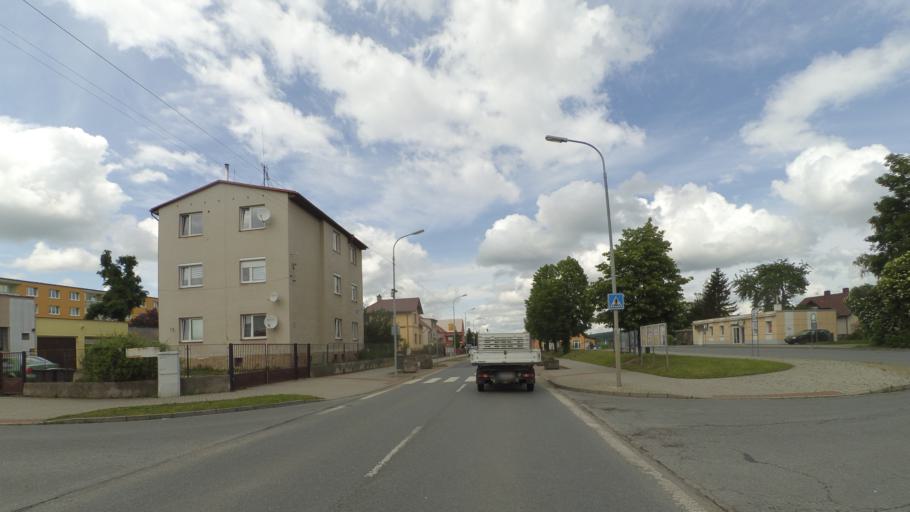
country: CZ
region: Plzensky
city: Bor
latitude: 49.7146
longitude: 12.7774
